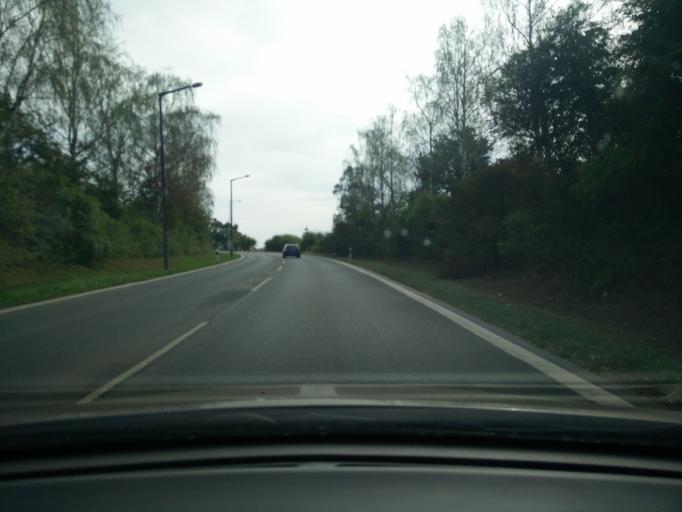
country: DE
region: Bavaria
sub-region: Regierungsbezirk Mittelfranken
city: Zirndorf
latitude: 49.4846
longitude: 10.9319
